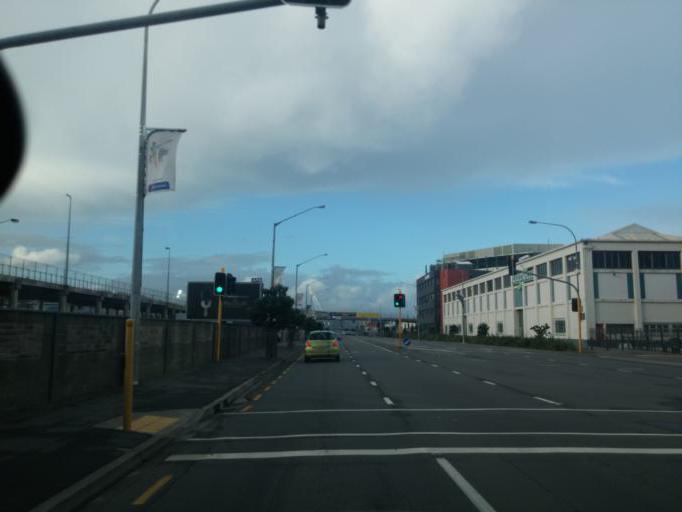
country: NZ
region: Wellington
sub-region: Wellington City
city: Wellington
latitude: -41.2786
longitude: 174.7818
